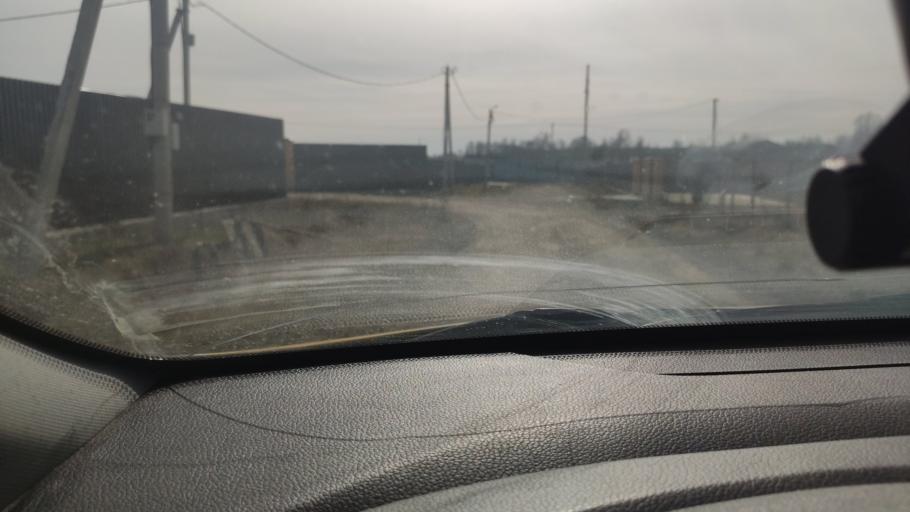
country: RU
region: Moskovskaya
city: Ruza
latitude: 55.7636
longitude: 36.1282
